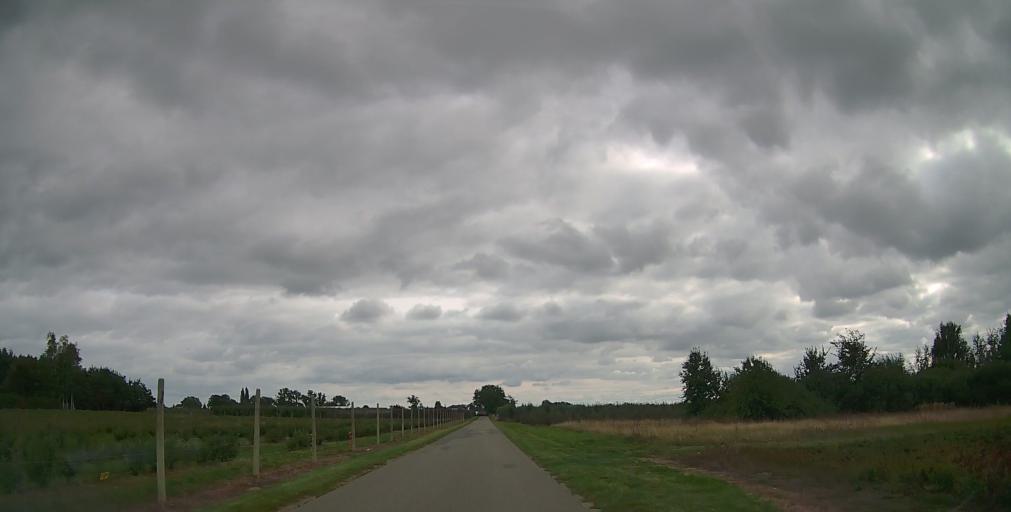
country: PL
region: Masovian Voivodeship
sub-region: Powiat grojecki
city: Goszczyn
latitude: 51.7630
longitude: 20.8702
